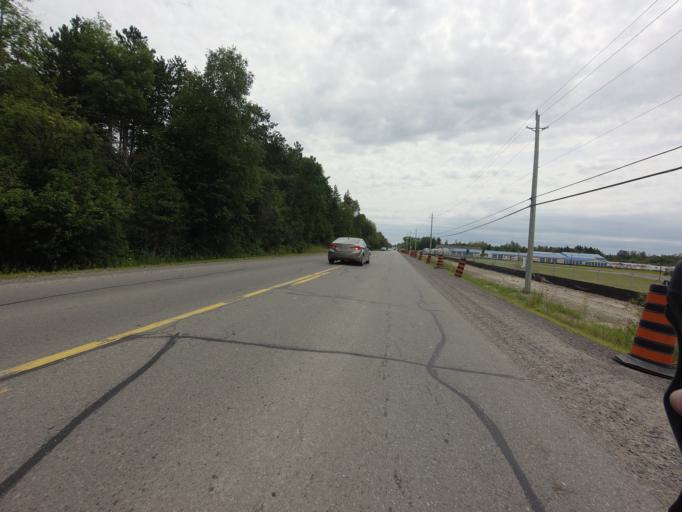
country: CA
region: Ontario
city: Bells Corners
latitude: 45.0312
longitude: -75.6620
